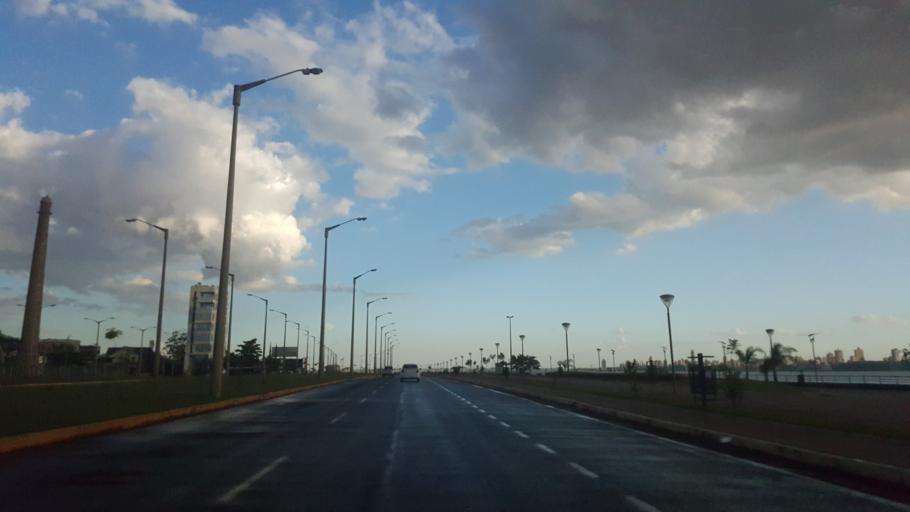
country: PY
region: Itapua
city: Encarnacion
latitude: -27.3292
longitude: -55.8755
